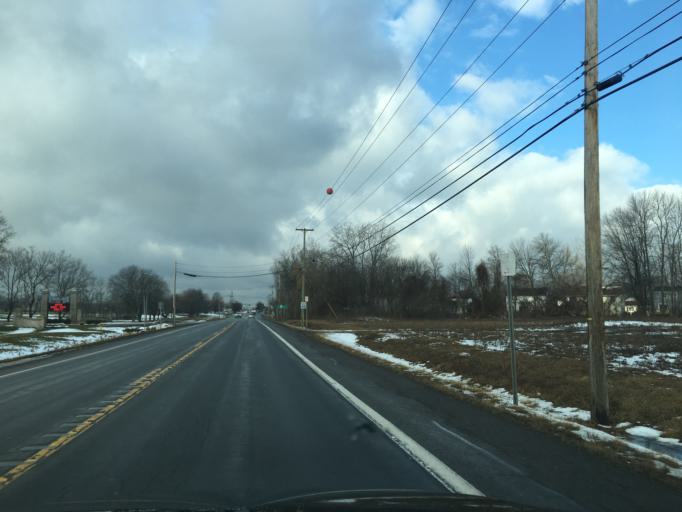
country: US
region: New York
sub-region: Ontario County
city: Victor
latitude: 42.9745
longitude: -77.3438
